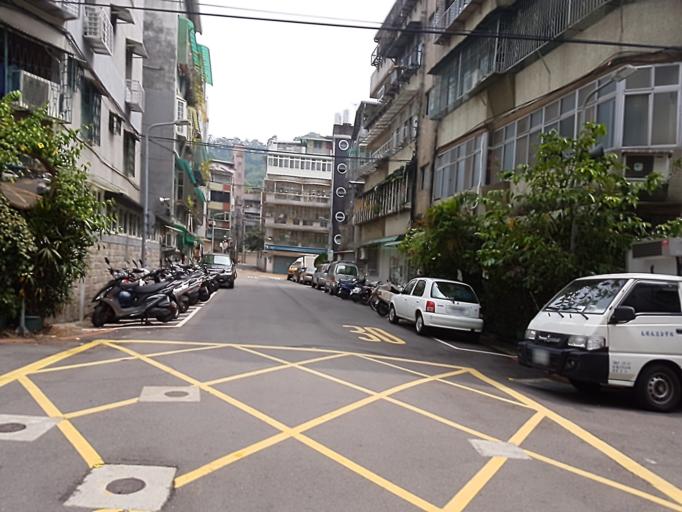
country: TW
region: Taipei
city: Taipei
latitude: 24.9967
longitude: 121.5463
